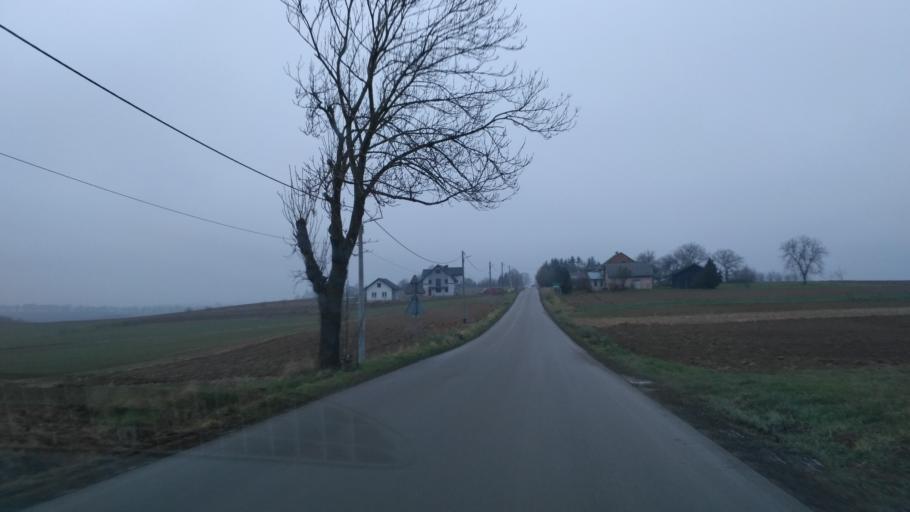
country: PL
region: Subcarpathian Voivodeship
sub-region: Powiat przeworski
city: Zurawiczki
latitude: 50.0002
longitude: 22.5016
